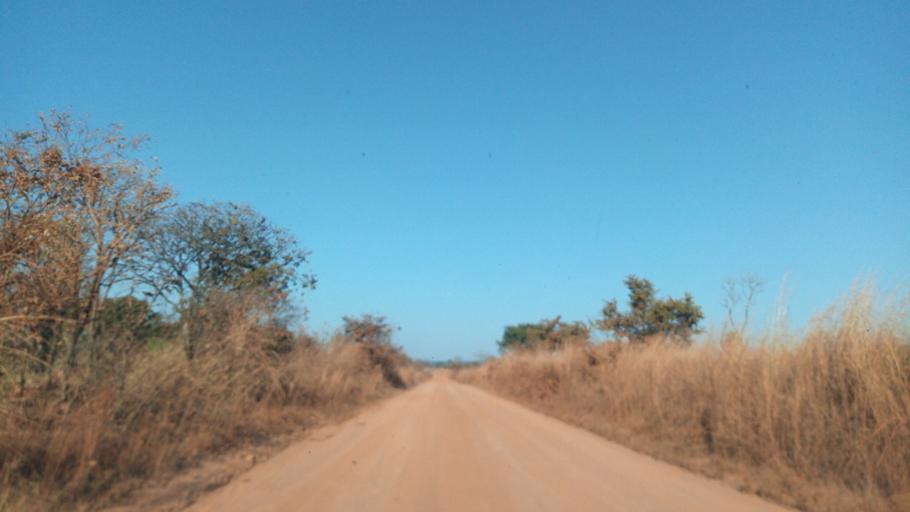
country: ZM
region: Luapula
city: Mwense
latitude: -10.5104
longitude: 28.4686
